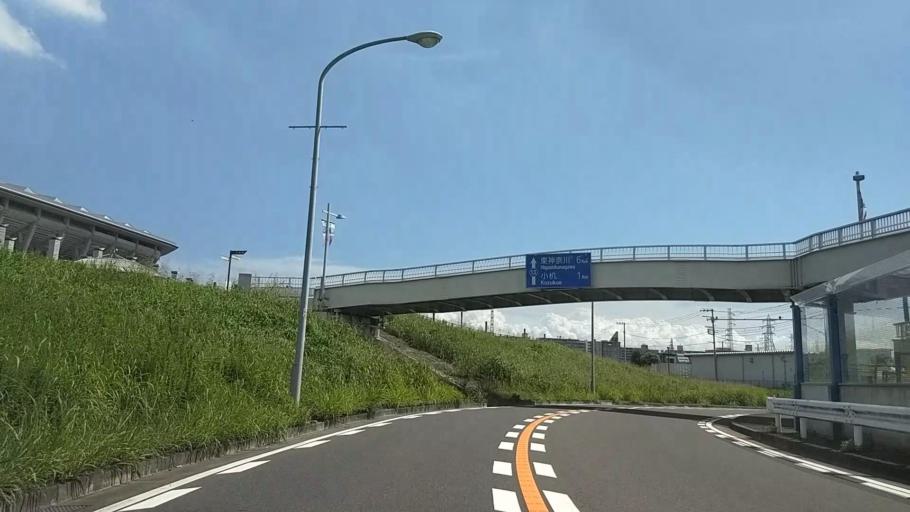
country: JP
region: Kanagawa
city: Yokohama
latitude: 35.5093
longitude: 139.6035
